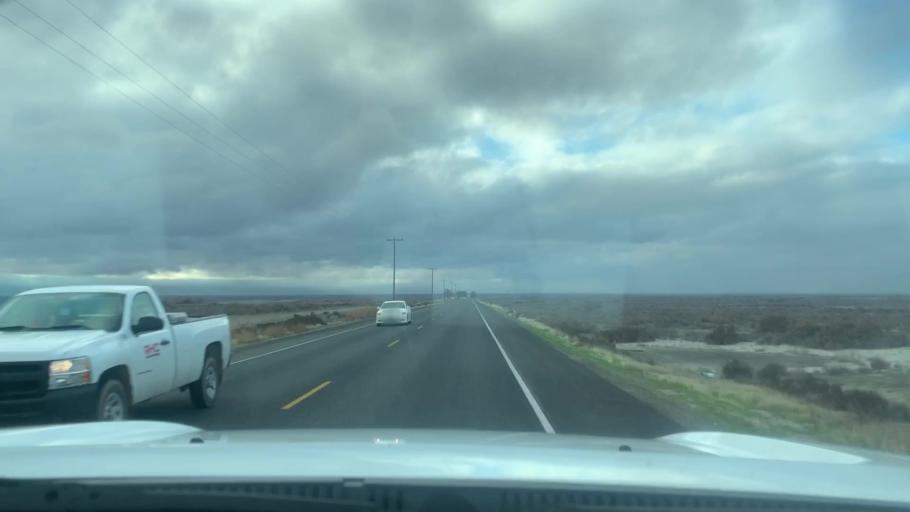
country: US
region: California
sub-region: Kern County
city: Buttonwillow
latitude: 35.4995
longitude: -119.5556
